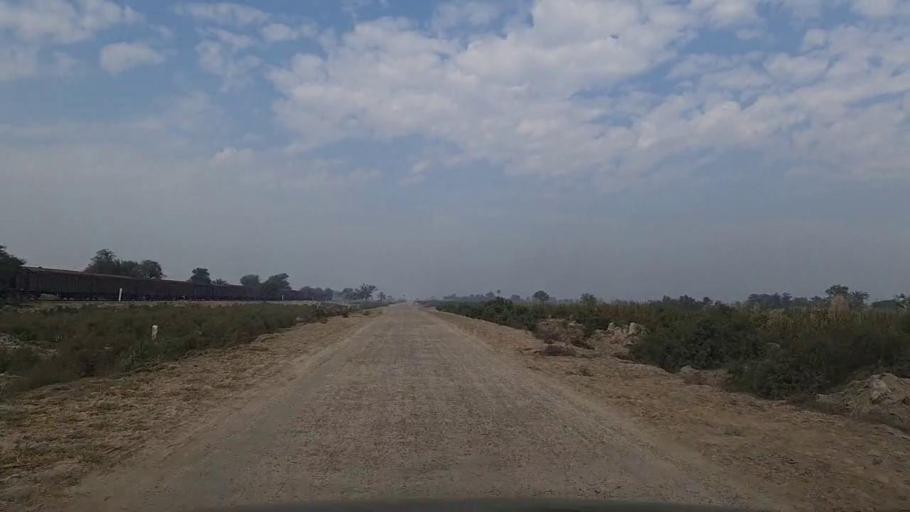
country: PK
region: Sindh
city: Daur
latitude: 26.3775
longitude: 68.3560
